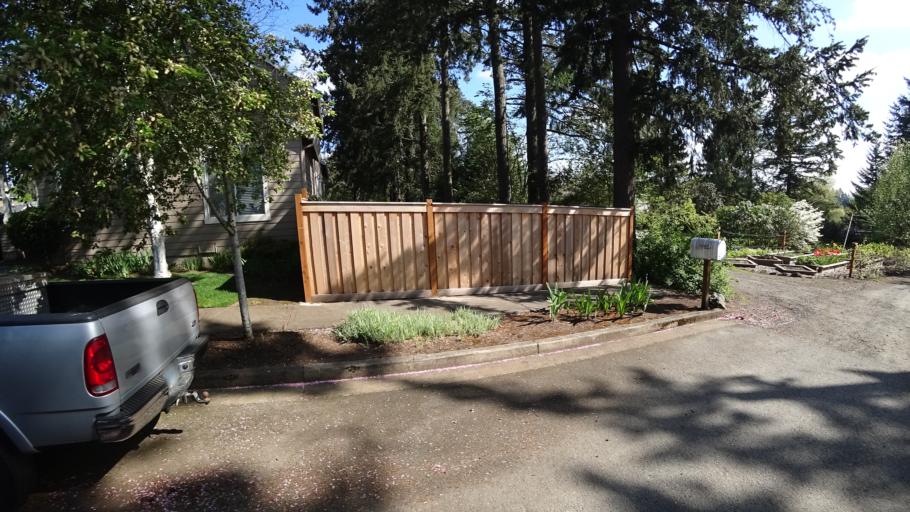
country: US
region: Oregon
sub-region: Washington County
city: King City
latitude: 45.4441
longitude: -122.8312
